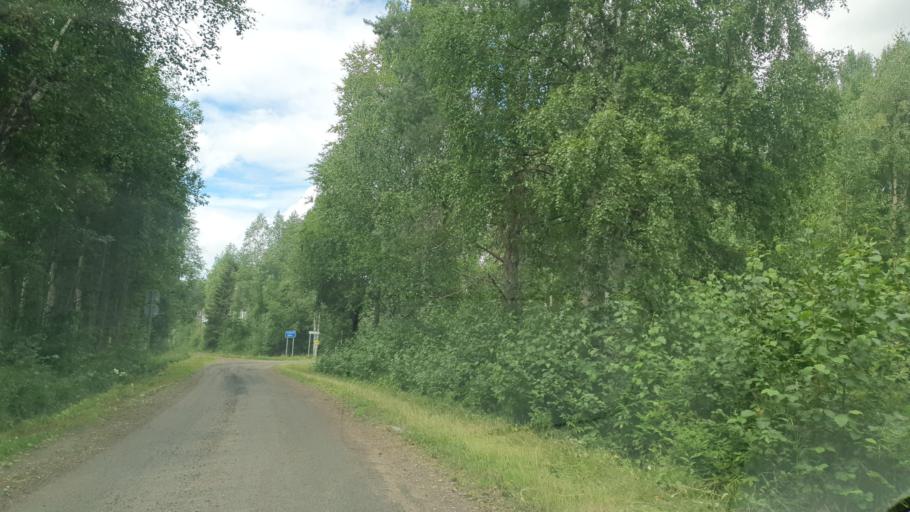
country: FI
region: Kainuu
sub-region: Kehys-Kainuu
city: Kuhmo
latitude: 64.0880
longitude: 29.0949
